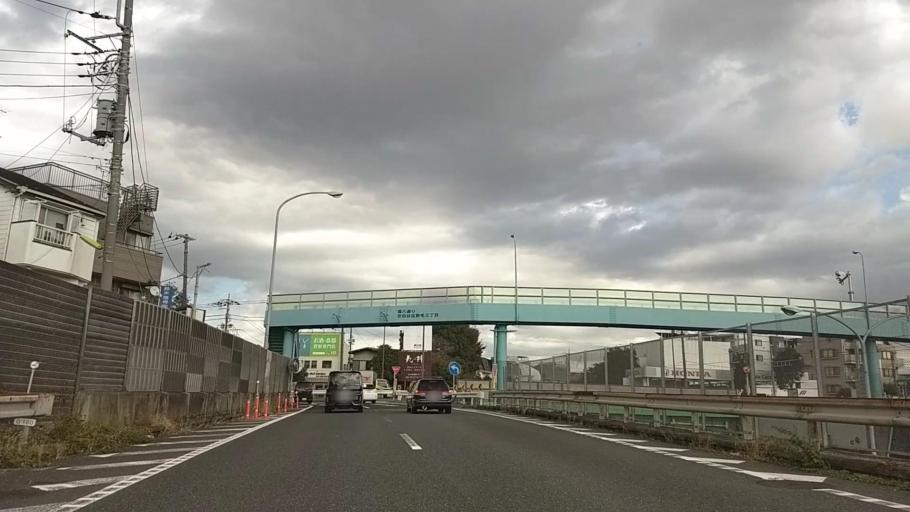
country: JP
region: Tokyo
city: Tokyo
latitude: 35.6069
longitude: 139.6401
